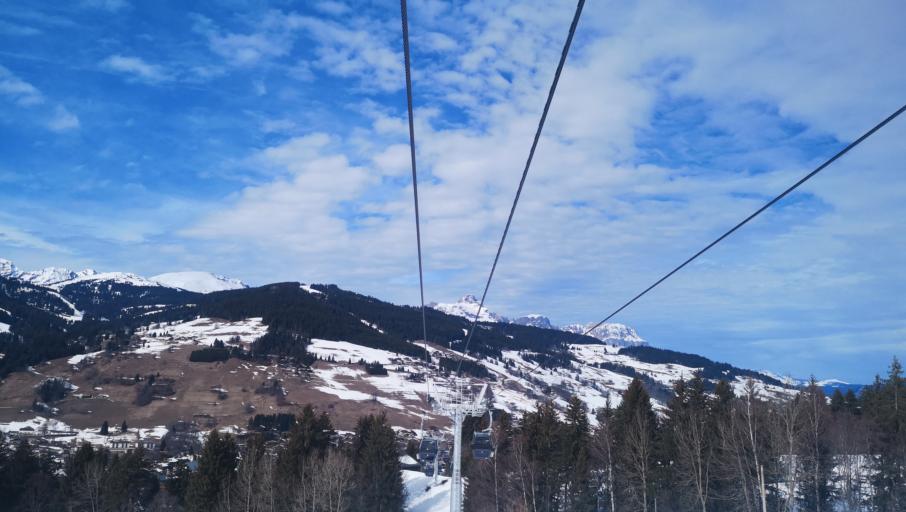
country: FR
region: Rhone-Alpes
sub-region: Departement de la Haute-Savoie
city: Megeve
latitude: 45.8477
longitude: 6.6236
